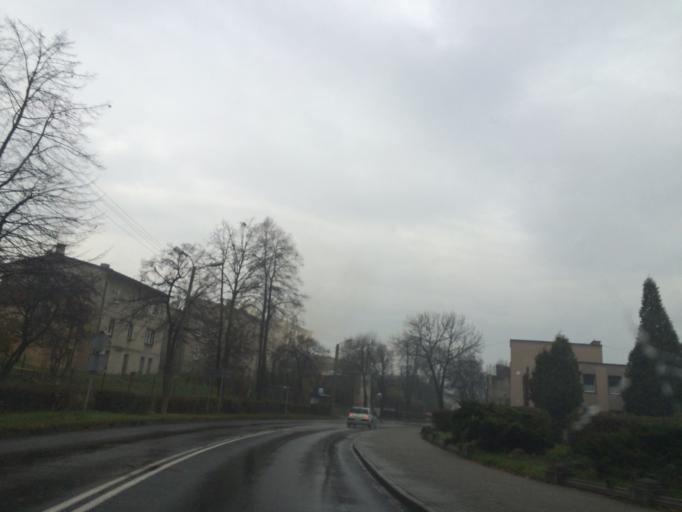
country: PL
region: Silesian Voivodeship
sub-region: Powiat tarnogorski
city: Radzionkow
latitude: 50.3948
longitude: 18.8993
